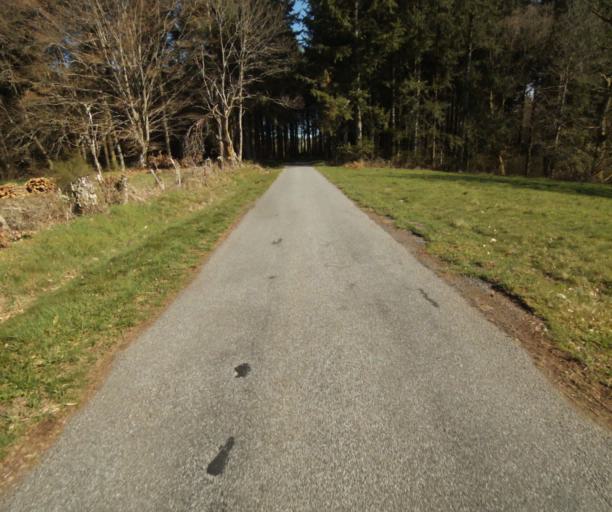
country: FR
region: Limousin
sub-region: Departement de la Correze
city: Correze
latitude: 45.2898
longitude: 1.9184
